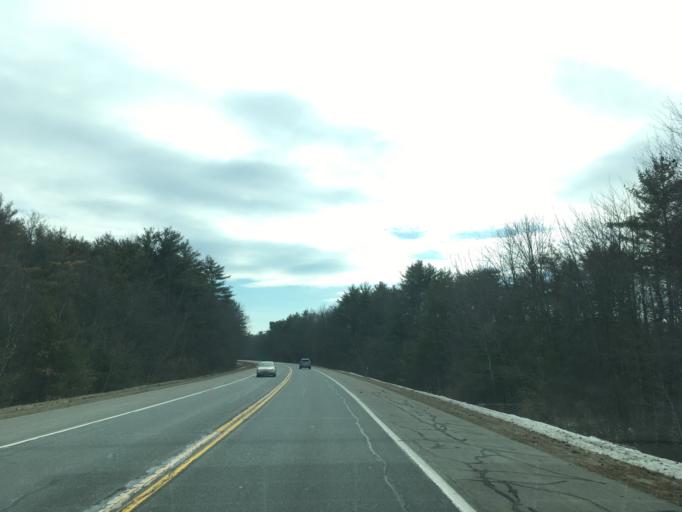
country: US
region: New Hampshire
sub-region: Rockingham County
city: Hampton
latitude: 42.9430
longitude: -70.8504
